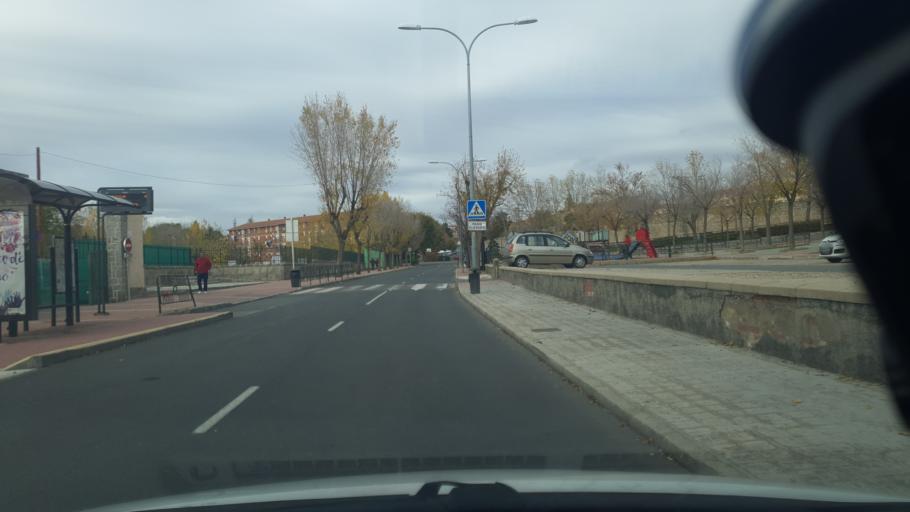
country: ES
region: Castille and Leon
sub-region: Provincia de Avila
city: Avila
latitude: 40.6475
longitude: -4.6859
